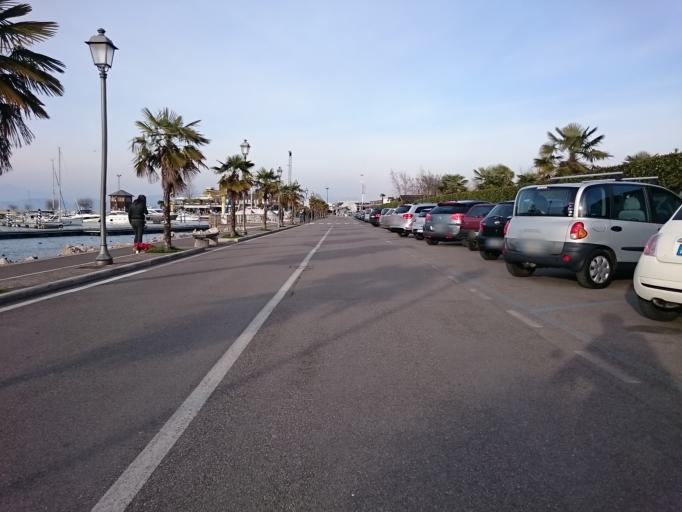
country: IT
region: Veneto
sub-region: Provincia di Verona
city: Peschiera del Garda
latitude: 45.4457
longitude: 10.6947
